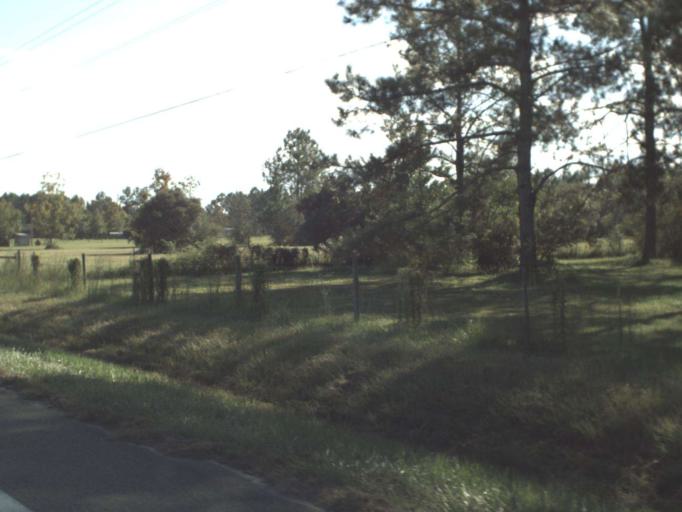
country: US
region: Florida
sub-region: Gulf County
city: Wewahitchka
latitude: 30.0256
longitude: -85.1800
